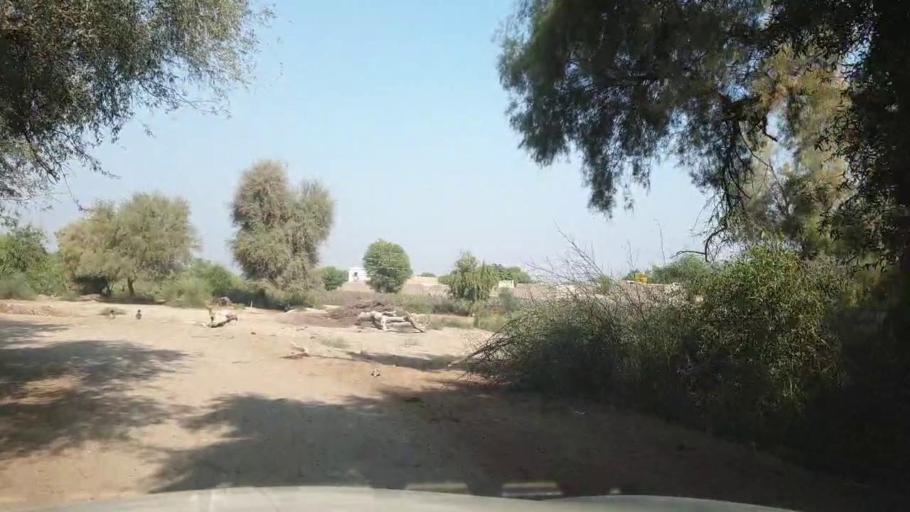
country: PK
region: Sindh
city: Bhan
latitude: 26.5151
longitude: 67.7743
